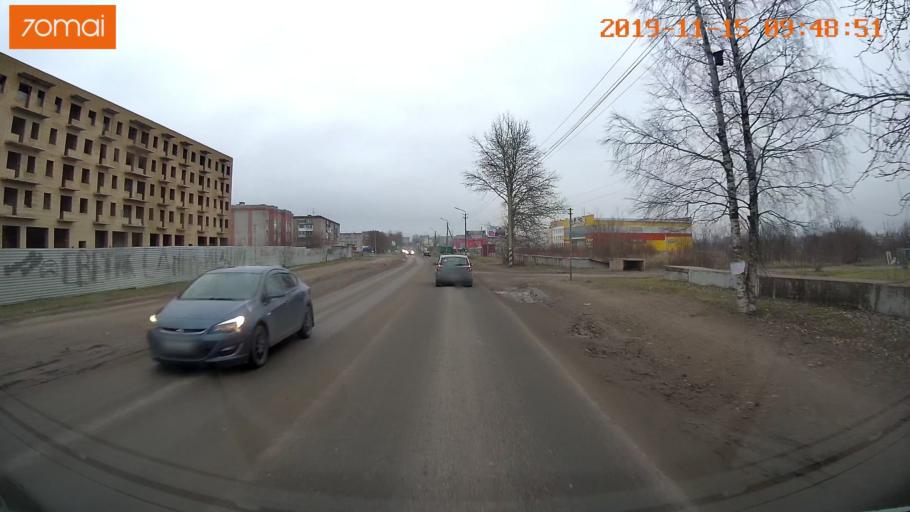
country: RU
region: Vologda
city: Sheksna
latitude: 59.2256
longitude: 38.5137
